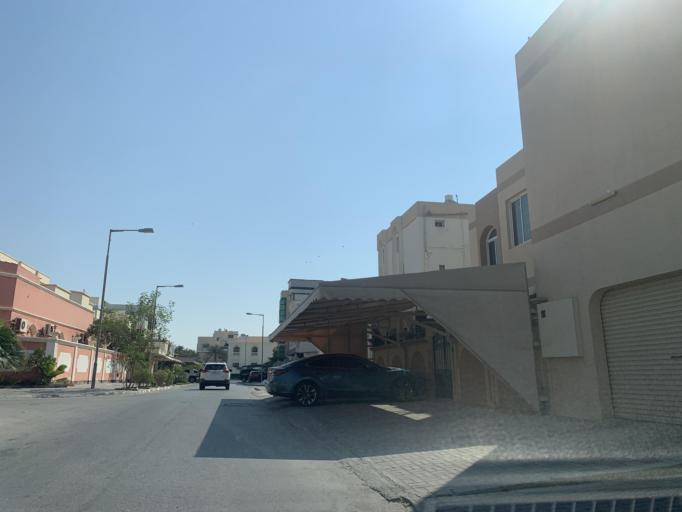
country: BH
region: Central Governorate
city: Madinat Hamad
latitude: 26.1114
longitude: 50.4972
